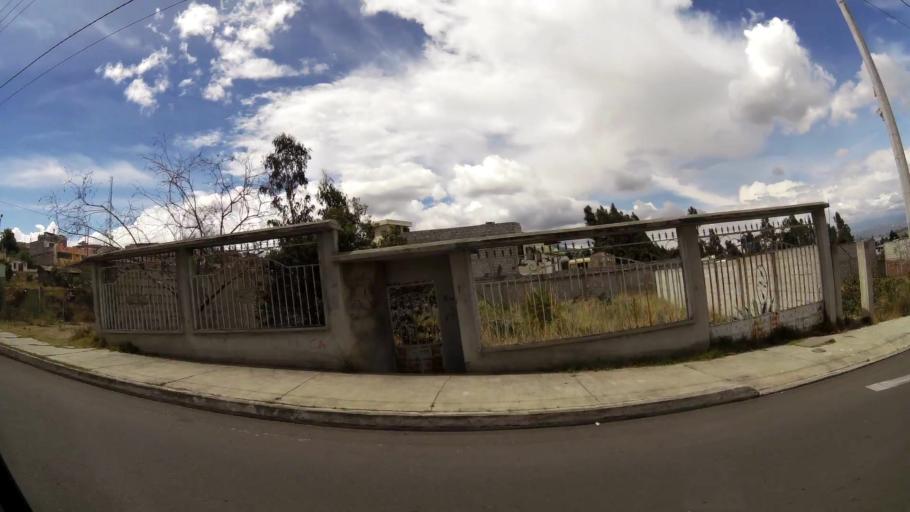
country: EC
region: Tungurahua
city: Ambato
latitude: -1.2616
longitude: -78.6166
